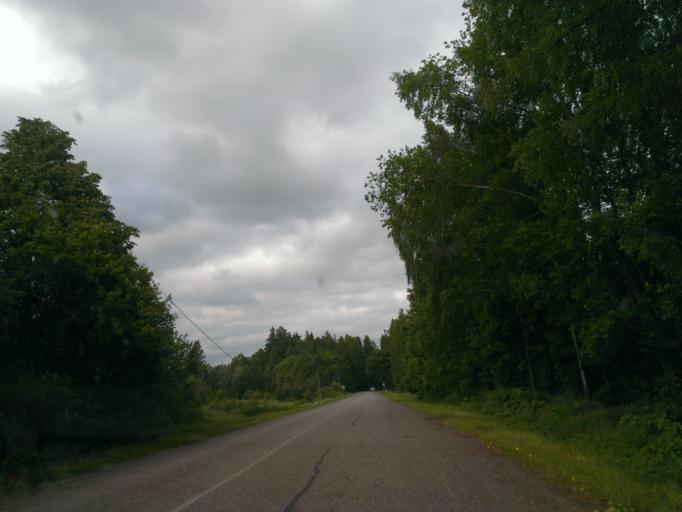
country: LV
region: Skrunda
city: Skrunda
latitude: 56.6914
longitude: 21.8669
